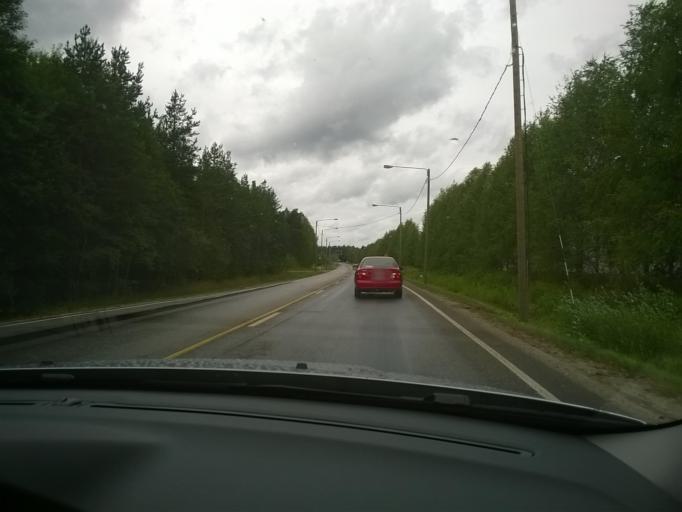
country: FI
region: Kainuu
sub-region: Kehys-Kainuu
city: Kuhmo
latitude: 64.1306
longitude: 29.4936
